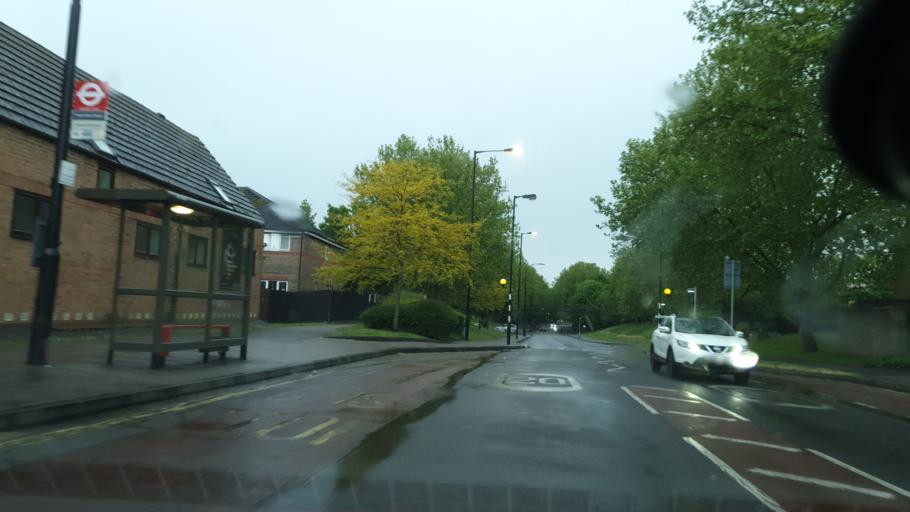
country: GB
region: England
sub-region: Greater London
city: Poplar
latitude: 51.5030
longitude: -0.0358
